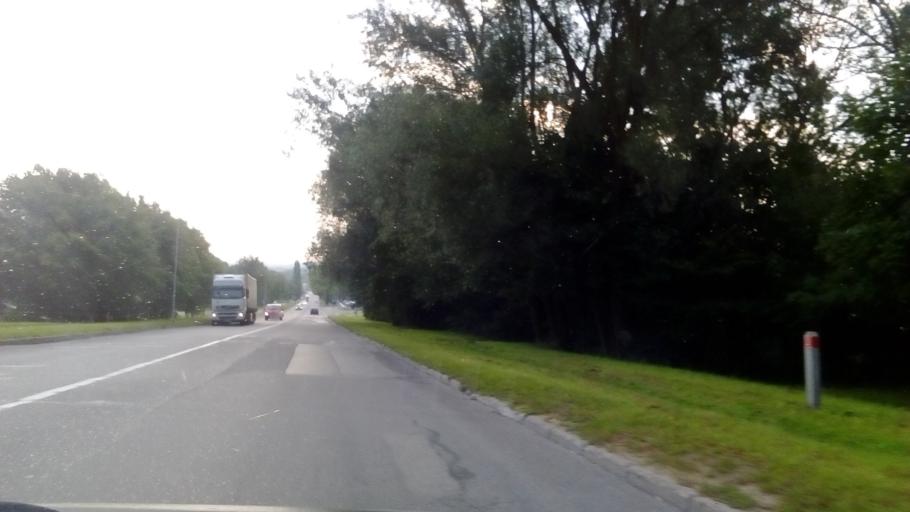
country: LT
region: Alytaus apskritis
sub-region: Alytus
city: Alytus
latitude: 54.3868
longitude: 24.0290
